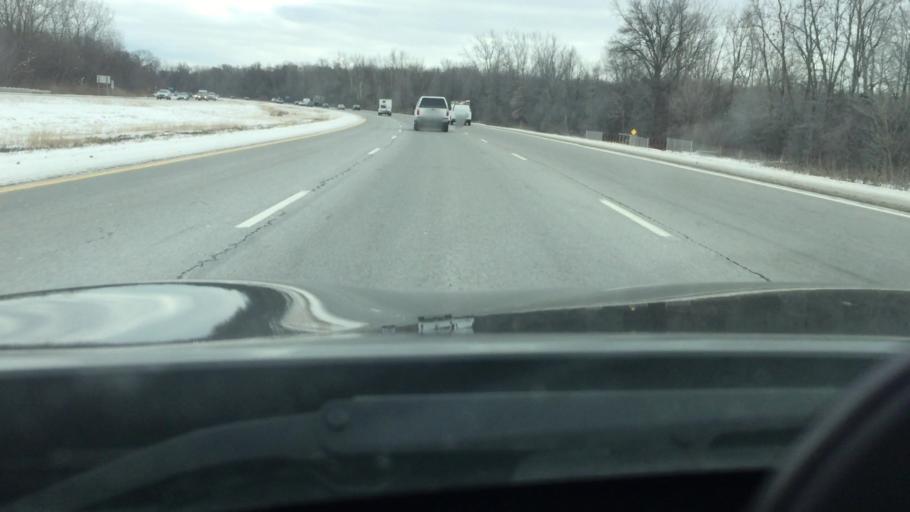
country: US
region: Michigan
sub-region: Wayne County
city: Romulus
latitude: 42.2351
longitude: -83.4379
